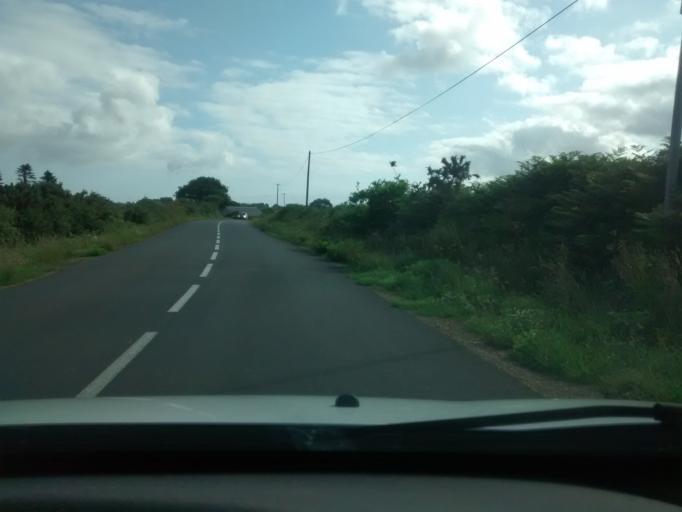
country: FR
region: Brittany
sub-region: Departement des Cotes-d'Armor
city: Louannec
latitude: 48.7882
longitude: -3.3900
